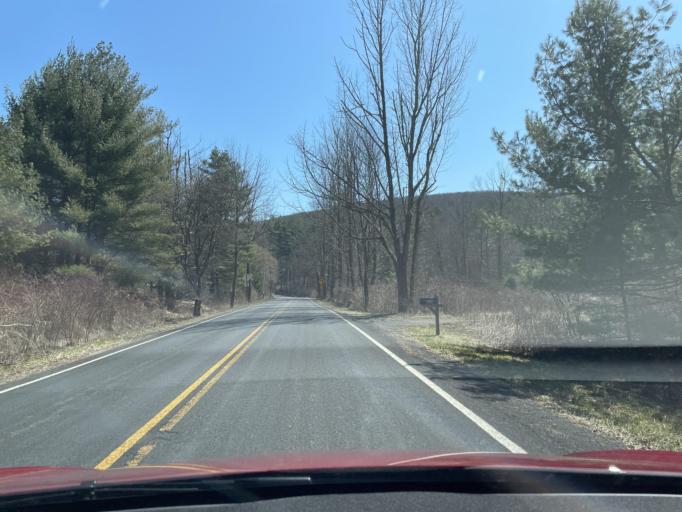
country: US
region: New York
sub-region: Ulster County
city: Shokan
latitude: 42.0185
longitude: -74.1874
